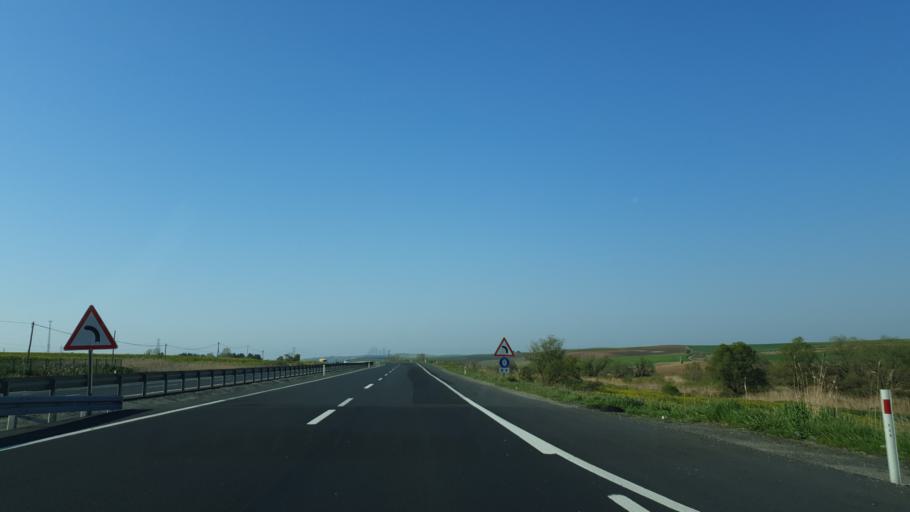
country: TR
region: Tekirdag
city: Corlu
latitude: 41.1198
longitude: 27.7507
